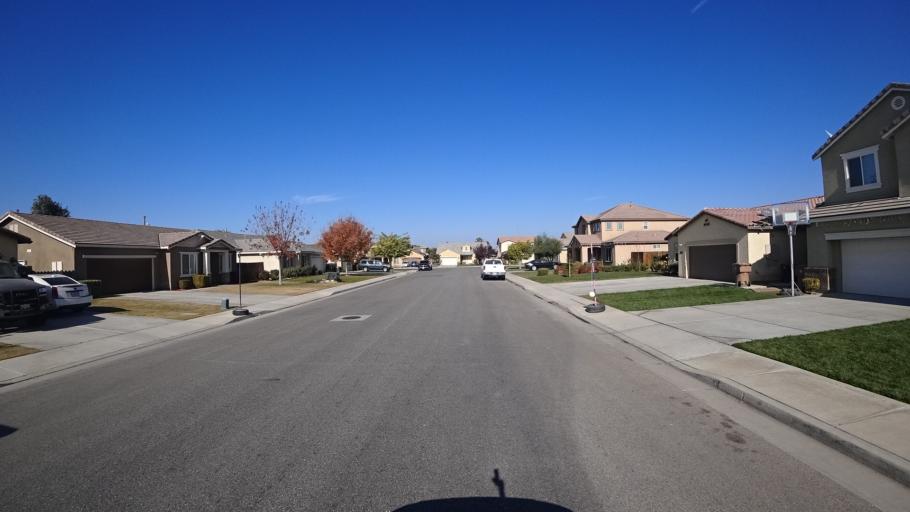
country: US
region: California
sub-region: Kern County
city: Greenfield
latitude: 35.2821
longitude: -119.0628
